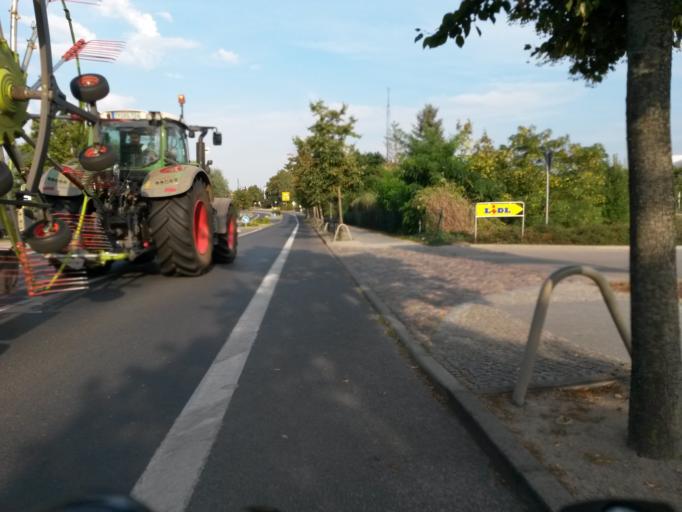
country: DE
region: Brandenburg
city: Templin
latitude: 53.1170
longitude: 13.5010
